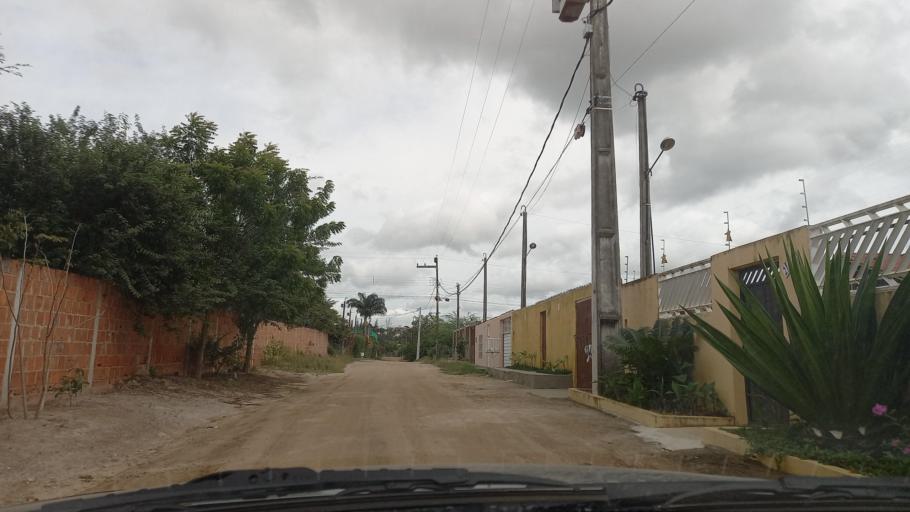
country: ET
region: Oromiya
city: Gore
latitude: 8.1899
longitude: 35.5832
